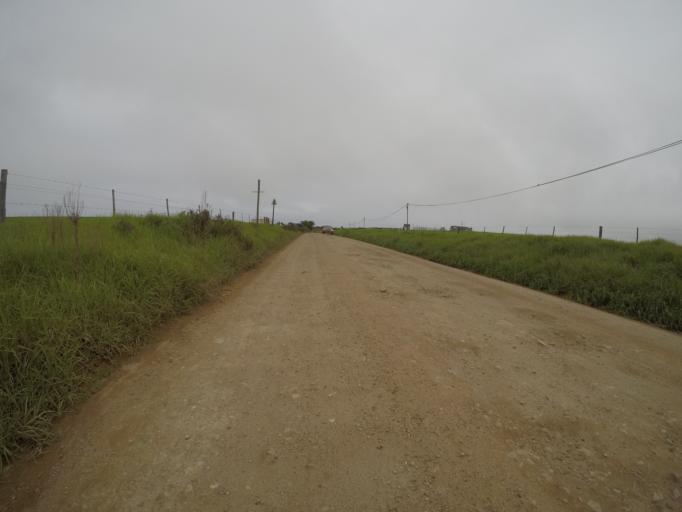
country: ZA
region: Eastern Cape
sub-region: Cacadu District Municipality
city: Kareedouw
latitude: -34.0694
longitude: 24.2375
